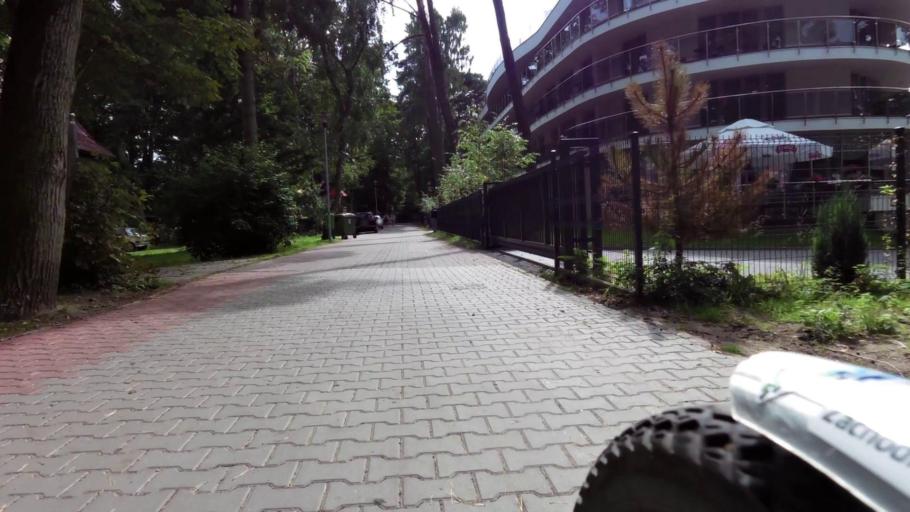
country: PL
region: West Pomeranian Voivodeship
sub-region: Powiat kolobrzeski
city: Ustronie Morskie
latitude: 54.2187
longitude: 15.7705
